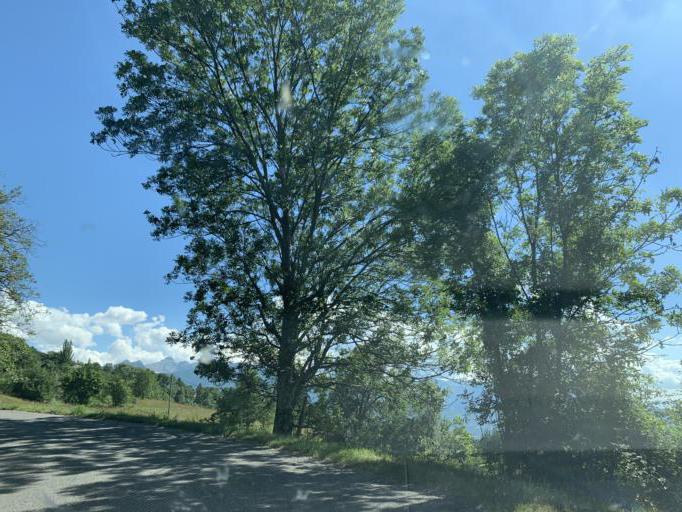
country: FR
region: Provence-Alpes-Cote d'Azur
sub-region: Departement des Hautes-Alpes
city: Embrun
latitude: 44.5857
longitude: 6.5330
